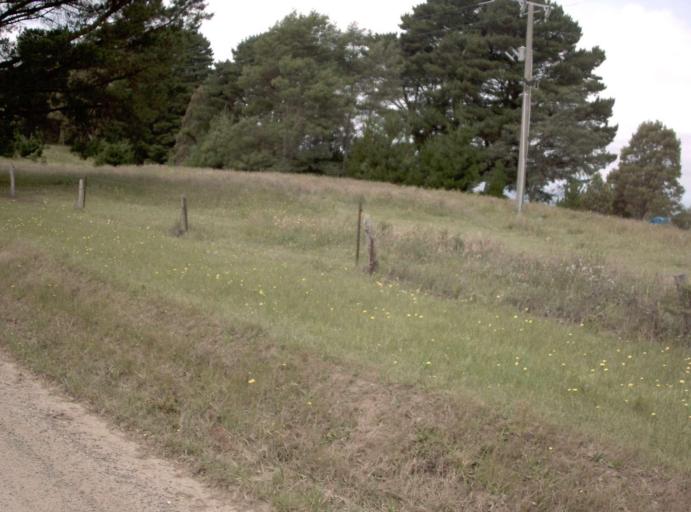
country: AU
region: Victoria
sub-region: Latrobe
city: Traralgon
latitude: -38.3730
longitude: 146.6873
